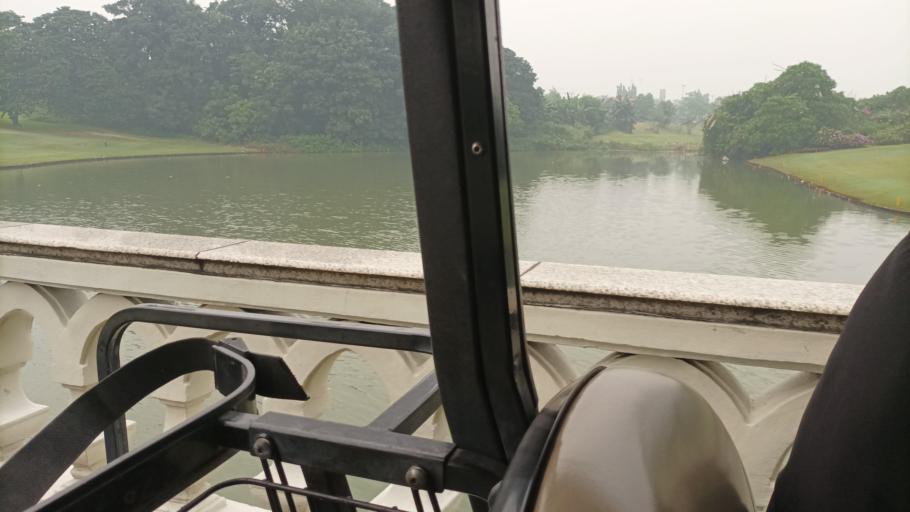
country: ID
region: West Java
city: Citeureup
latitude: -6.4185
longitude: 106.8938
